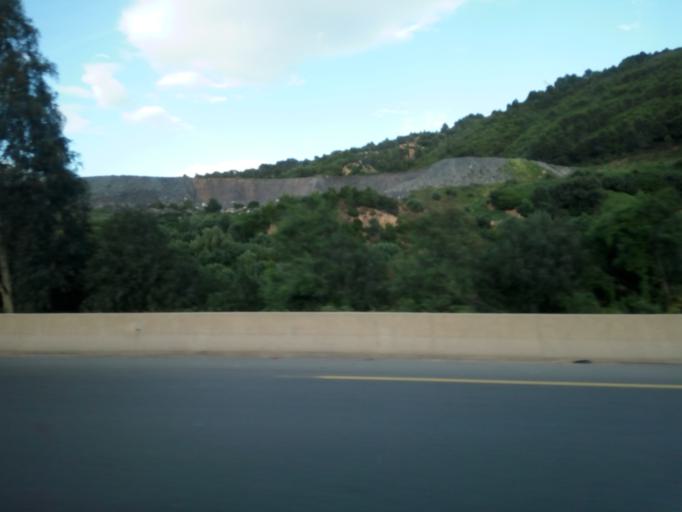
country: DZ
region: Tipaza
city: El Affroun
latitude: 36.4082
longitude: 2.5613
